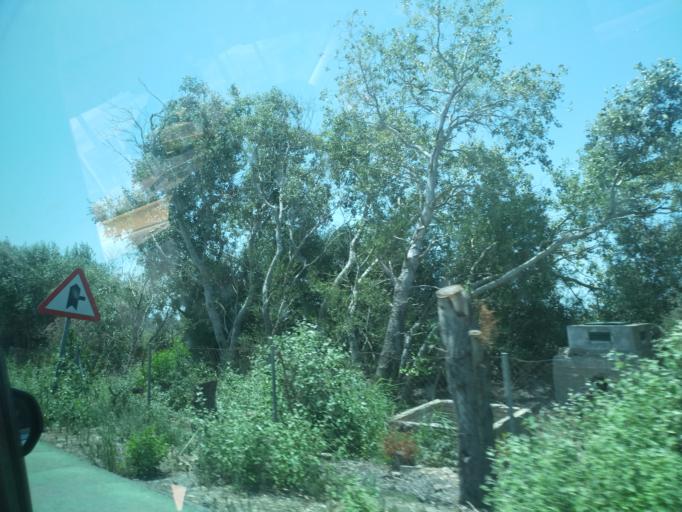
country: ES
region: Andalusia
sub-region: Provincia de Cadiz
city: Chiclana de la Frontera
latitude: 36.4341
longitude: -6.1435
